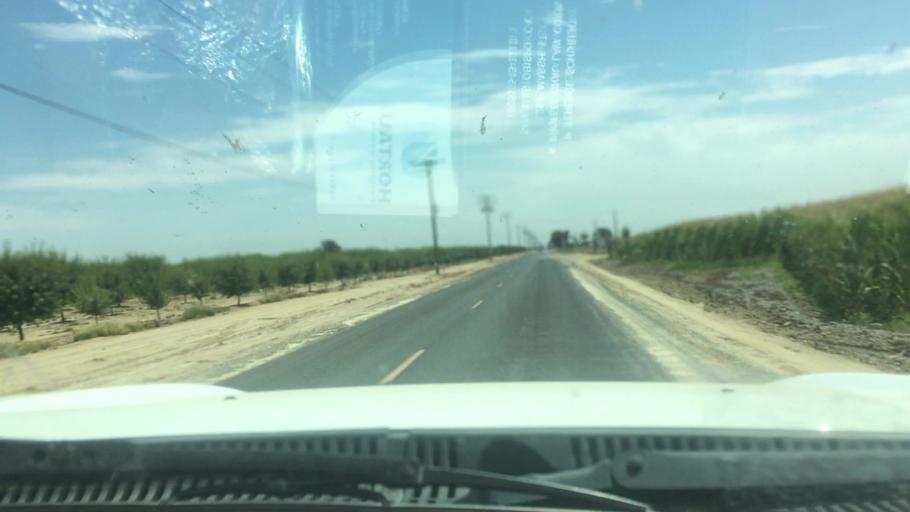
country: US
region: California
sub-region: Tulare County
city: Tipton
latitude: 36.0566
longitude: -119.3220
